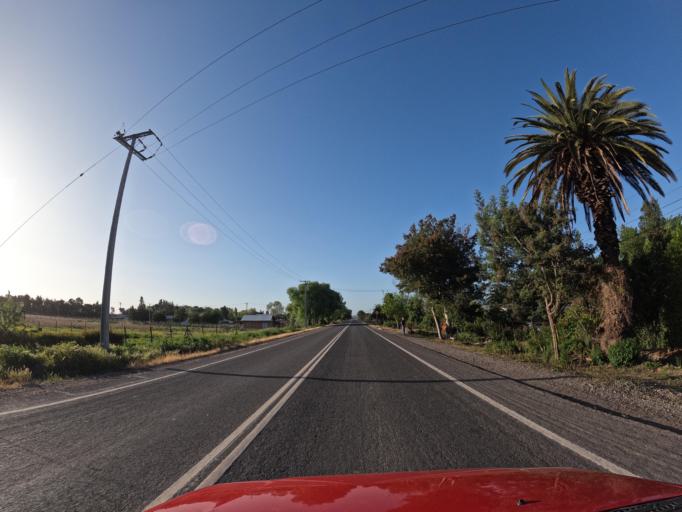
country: CL
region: O'Higgins
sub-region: Provincia de Colchagua
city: Santa Cruz
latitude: -34.4728
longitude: -71.3612
